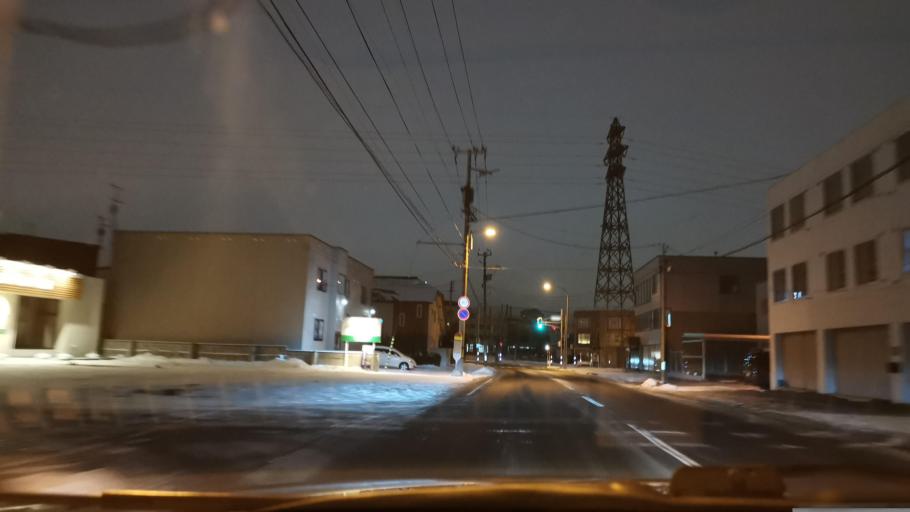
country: JP
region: Hokkaido
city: Sapporo
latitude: 43.0647
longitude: 141.4215
